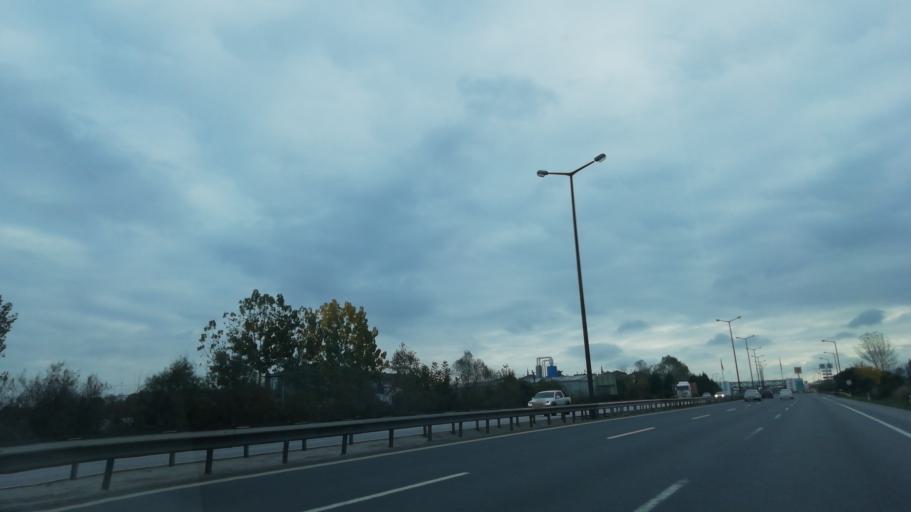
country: TR
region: Kocaeli
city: Derbent
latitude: 40.7295
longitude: 30.0631
